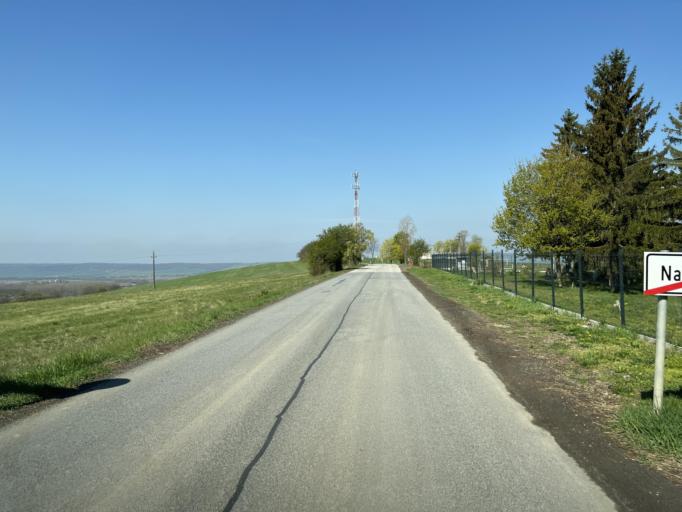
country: HU
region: Pest
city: Szob
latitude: 47.9365
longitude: 18.8172
